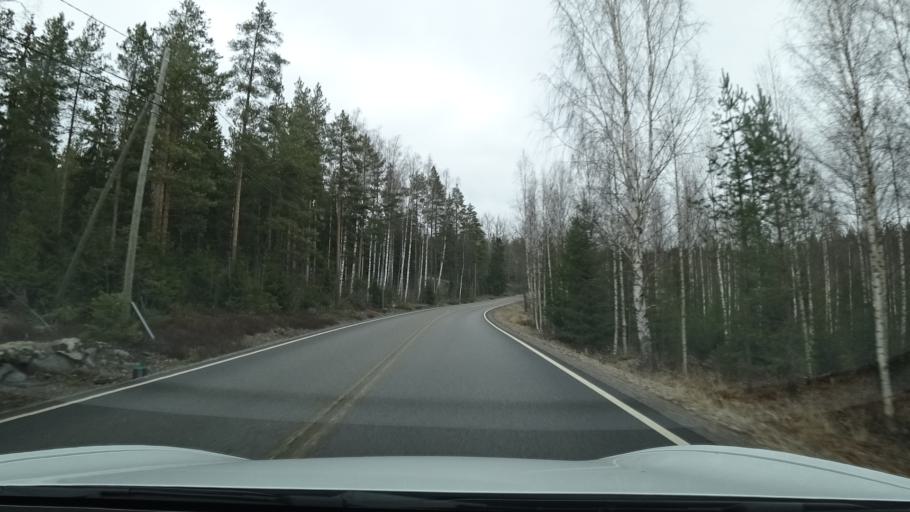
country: FI
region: Uusimaa
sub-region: Porvoo
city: Askola
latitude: 60.5734
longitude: 25.5846
